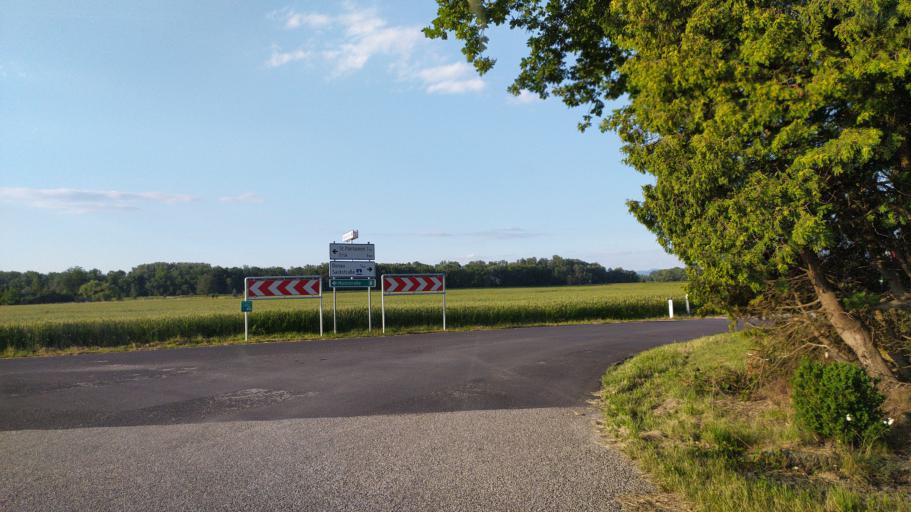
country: AT
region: Lower Austria
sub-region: Politischer Bezirk Amstetten
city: Strengberg
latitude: 48.1728
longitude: 14.6279
